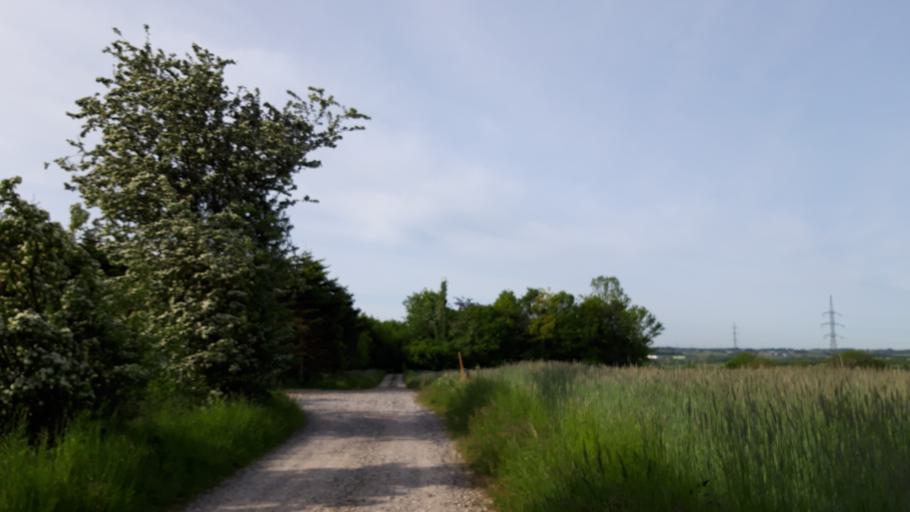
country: DK
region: Central Jutland
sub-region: Arhus Kommune
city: Lystrup
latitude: 56.2286
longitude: 10.1960
